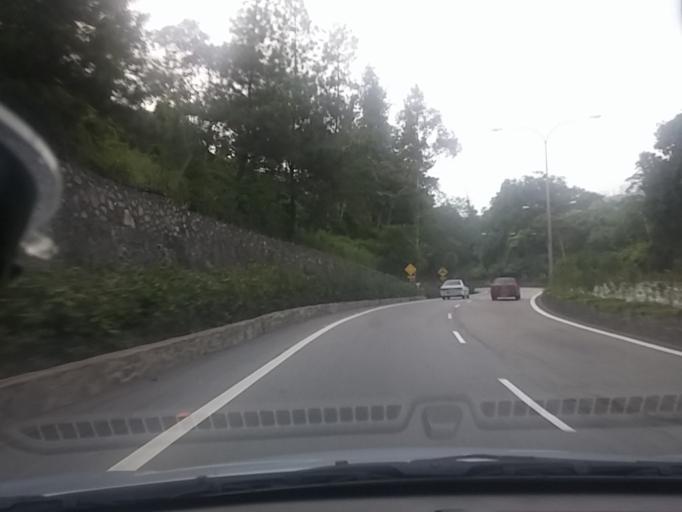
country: MY
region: Pahang
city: Kampung Bukit Tinggi, Bentong
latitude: 3.3950
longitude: 101.7694
